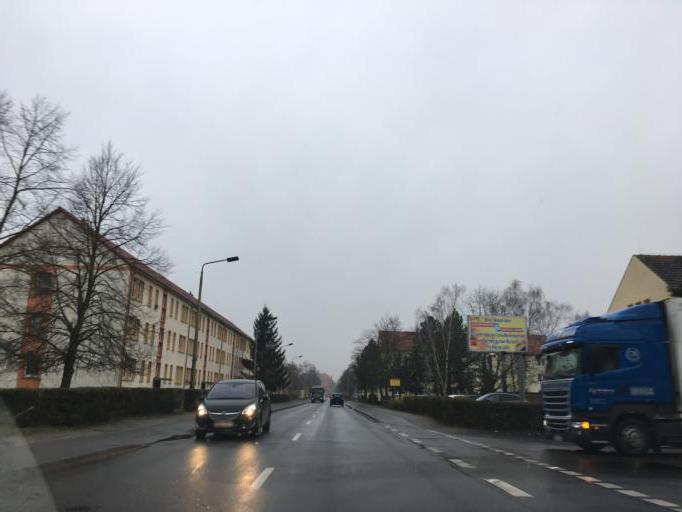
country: DE
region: Saxony-Anhalt
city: Haldensleben I
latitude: 52.2817
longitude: 11.4196
